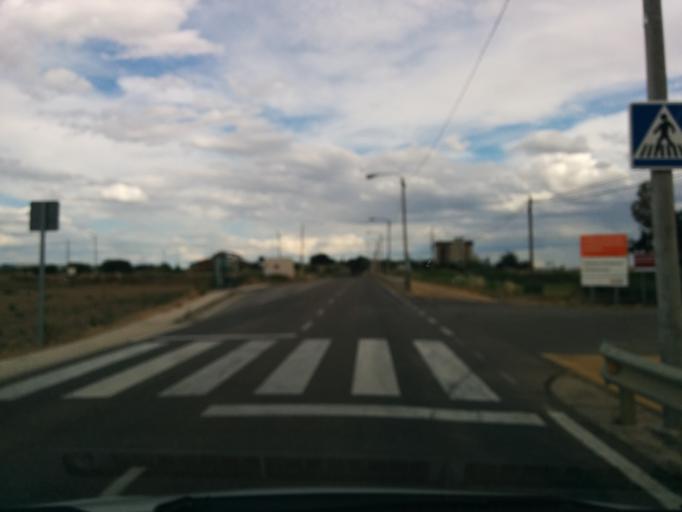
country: ES
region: Aragon
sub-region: Provincia de Zaragoza
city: Zaragoza
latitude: 41.6463
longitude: -0.8165
